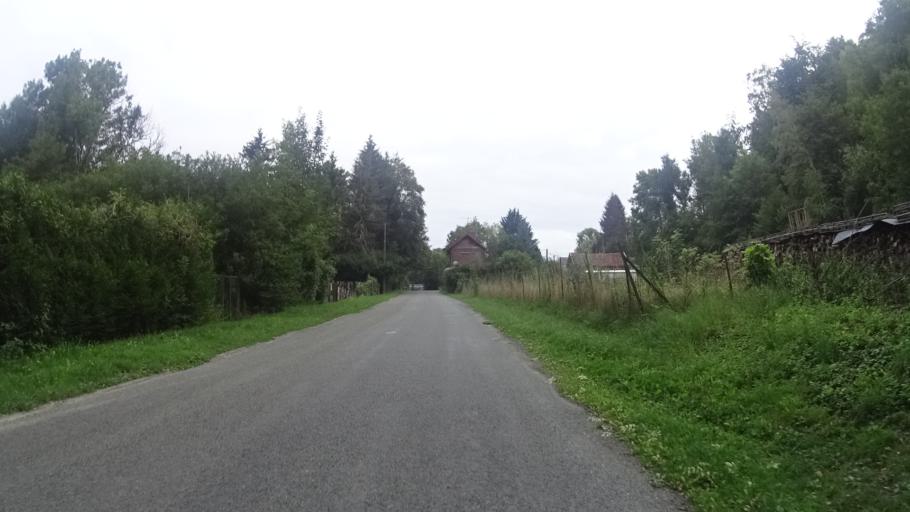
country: FR
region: Picardie
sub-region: Departement de l'Aisne
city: Guise
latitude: 49.8970
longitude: 3.5605
